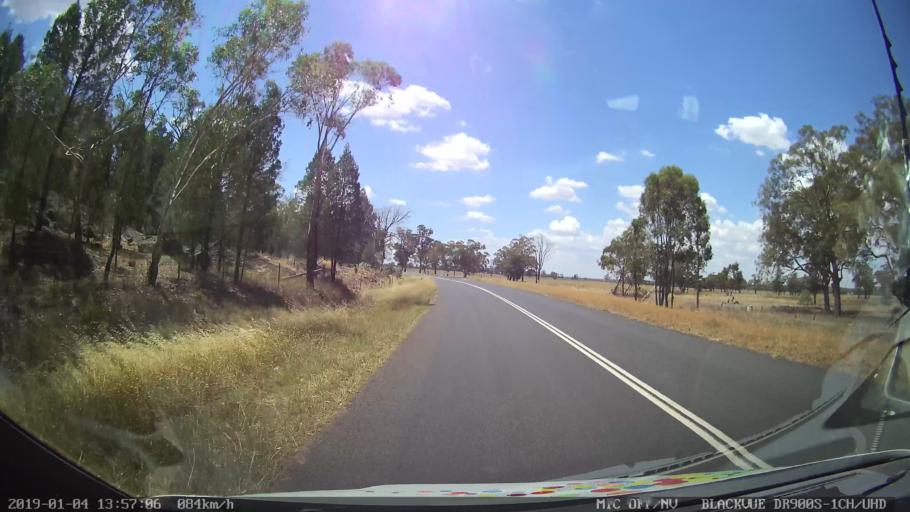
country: AU
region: New South Wales
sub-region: Dubbo Municipality
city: Dubbo
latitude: -32.3441
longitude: 148.5994
